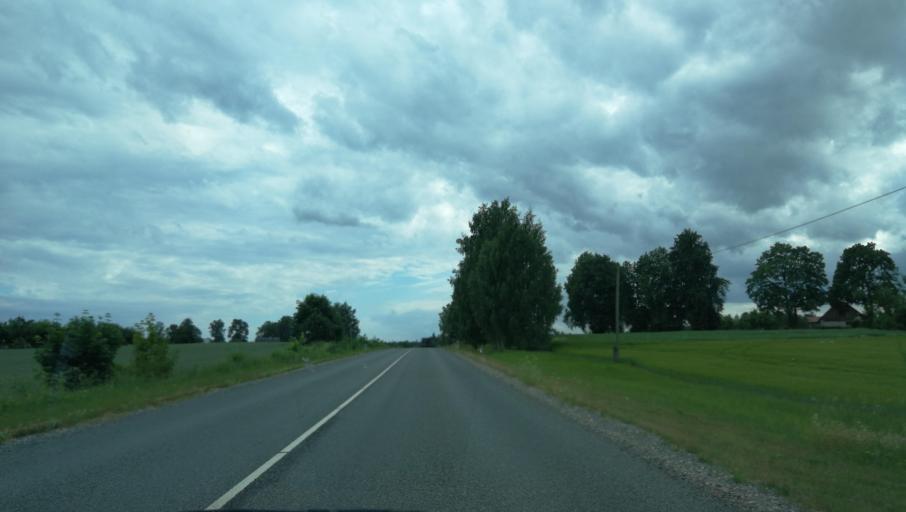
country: LV
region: Naukseni
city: Naukseni
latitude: 57.7371
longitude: 25.4269
